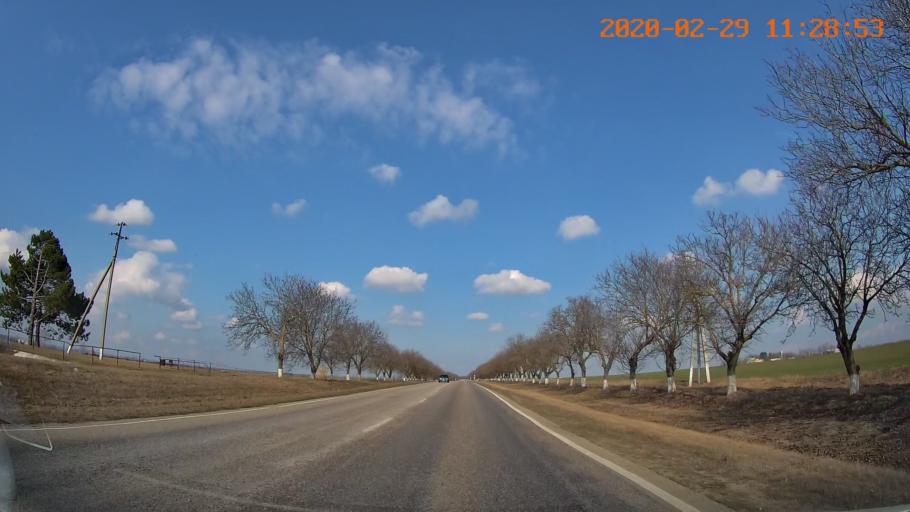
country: MD
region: Telenesti
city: Cocieri
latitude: 47.4859
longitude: 29.1303
